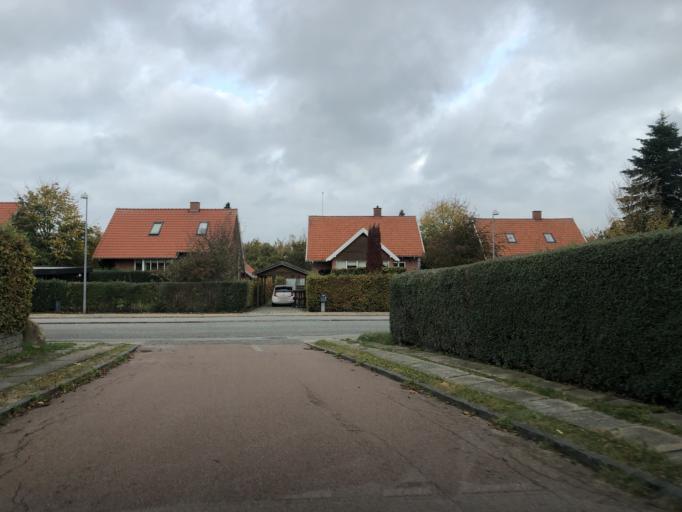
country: DK
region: Capital Region
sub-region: Rudersdal Kommune
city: Holte
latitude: 55.7912
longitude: 12.4665
